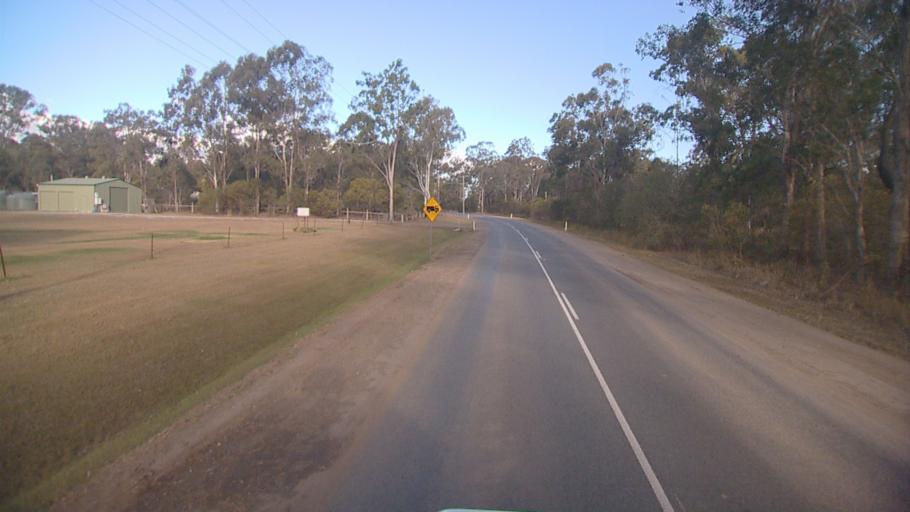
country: AU
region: Queensland
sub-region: Logan
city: Cedar Vale
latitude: -27.8605
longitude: 153.0558
